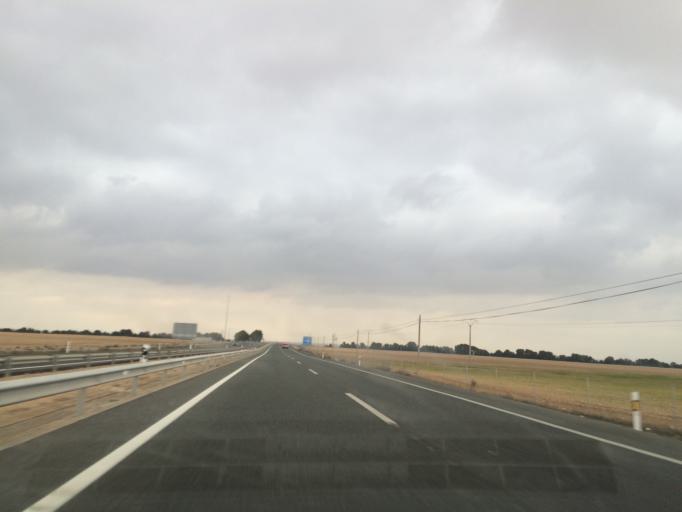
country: ES
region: Castille-La Mancha
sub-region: Province of Toledo
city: Tembleque
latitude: 39.6643
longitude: -3.5120
